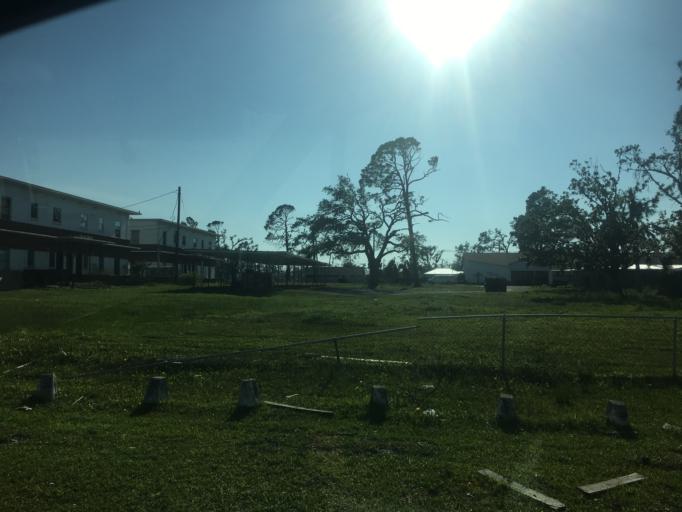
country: US
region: Florida
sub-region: Bay County
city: Panama City
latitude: 30.1465
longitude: -85.6483
